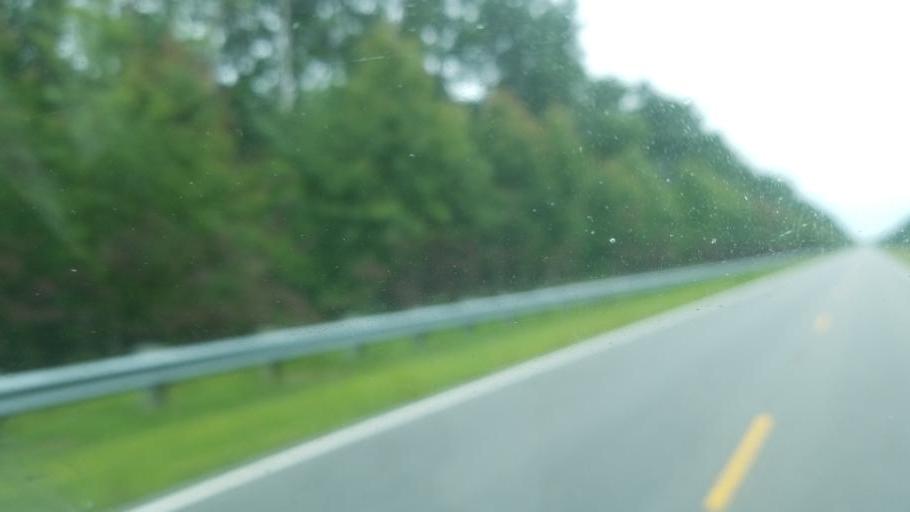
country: US
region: North Carolina
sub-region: Tyrrell County
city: Columbia
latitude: 35.9147
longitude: -76.1191
